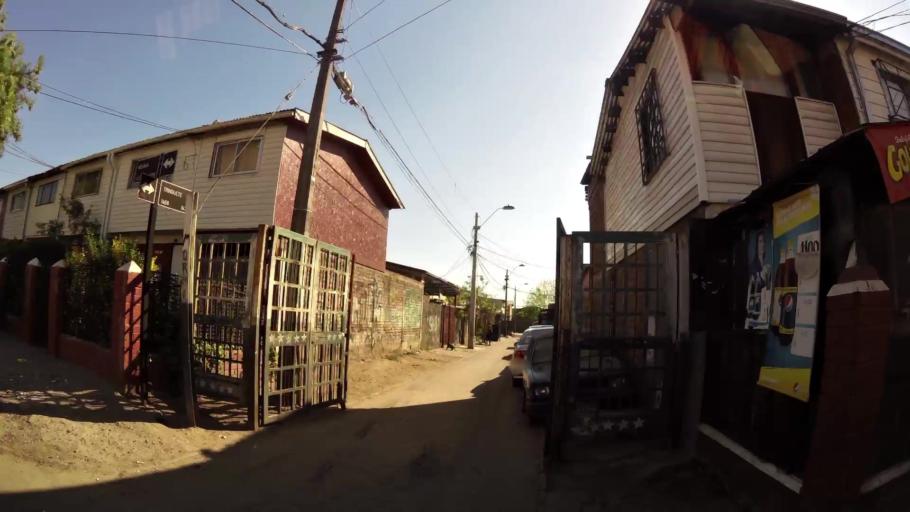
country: CL
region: Santiago Metropolitan
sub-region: Provincia de Santiago
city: La Pintana
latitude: -33.5644
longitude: -70.6086
